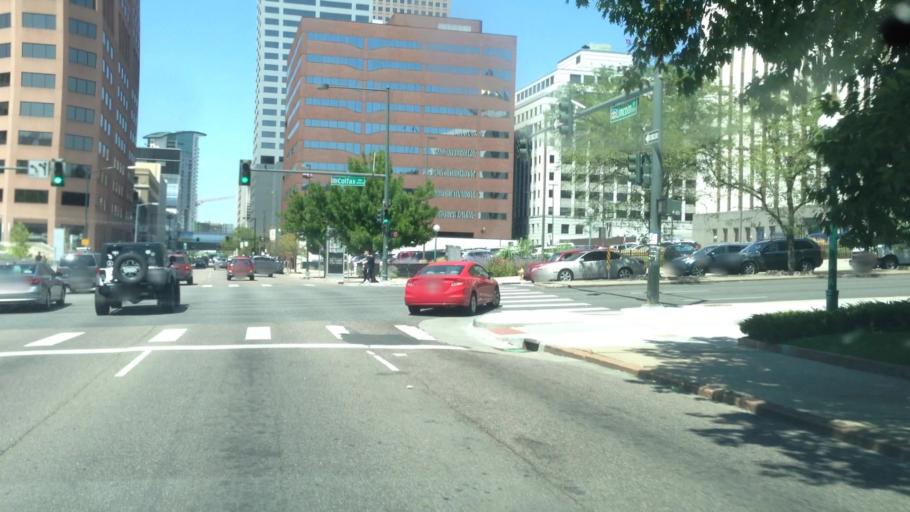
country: US
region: Colorado
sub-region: Denver County
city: Denver
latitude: 39.7398
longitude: -104.9861
